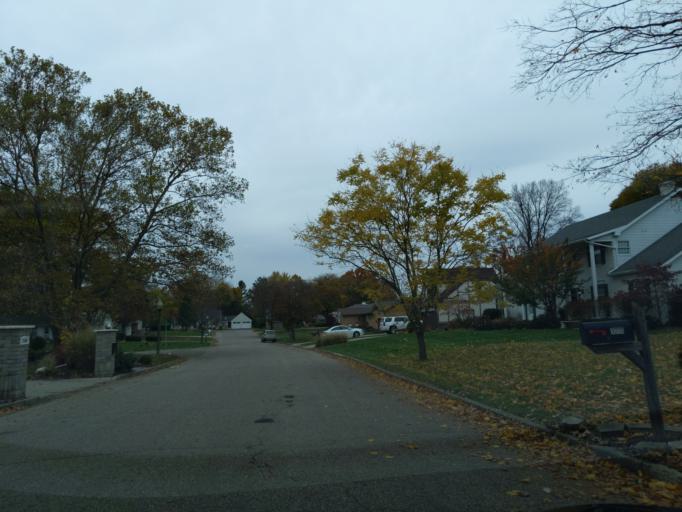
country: US
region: Michigan
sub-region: Ingham County
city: Edgemont Park
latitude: 42.7139
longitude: -84.5878
